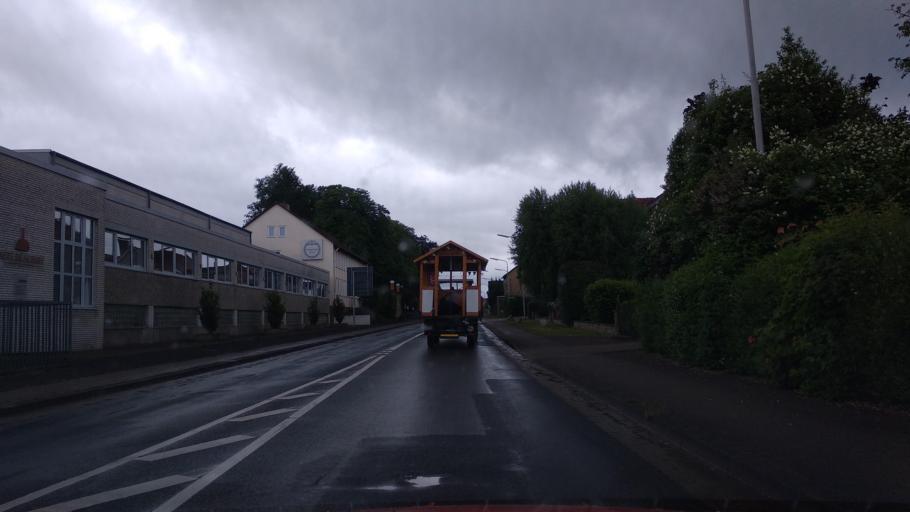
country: DE
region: Lower Saxony
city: Stadthagen
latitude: 52.3159
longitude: 9.2019
